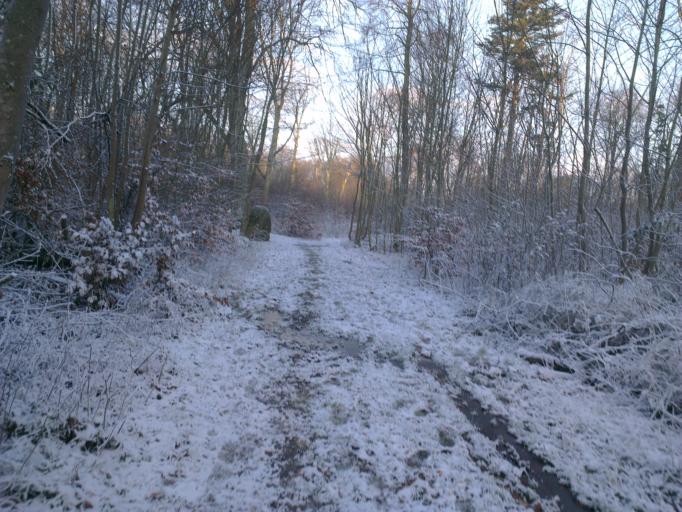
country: DK
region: Capital Region
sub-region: Frederikssund Kommune
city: Jaegerspris
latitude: 55.8675
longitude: 11.9854
